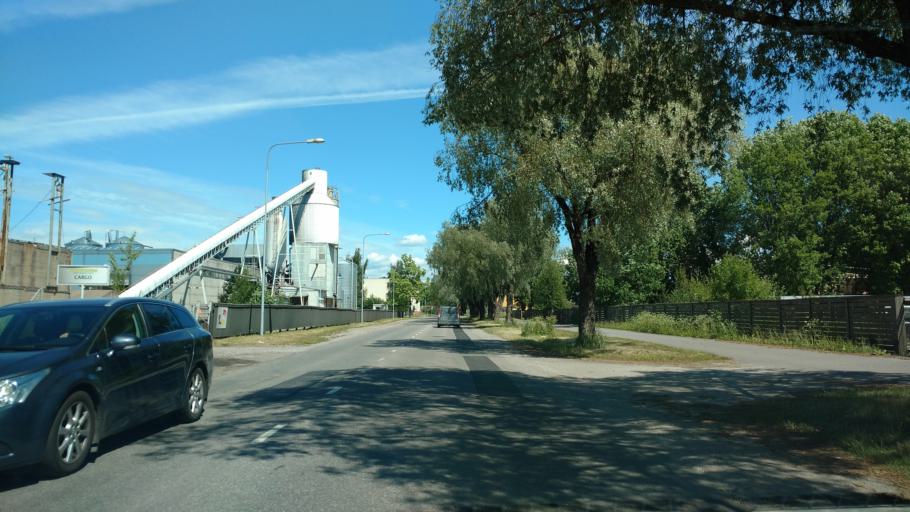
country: FI
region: Varsinais-Suomi
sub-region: Salo
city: Salo
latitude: 60.3806
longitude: 23.1176
